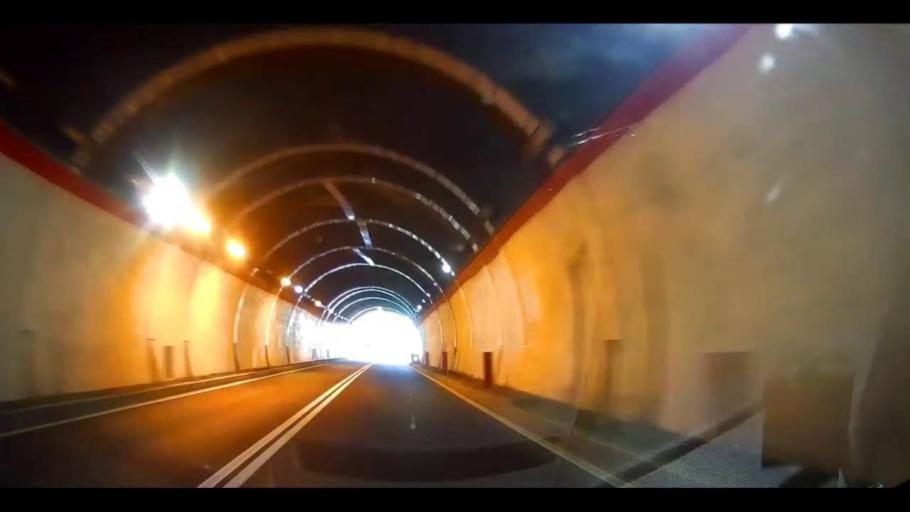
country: IT
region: Calabria
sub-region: Provincia di Cosenza
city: Celico
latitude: 39.3042
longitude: 16.3543
